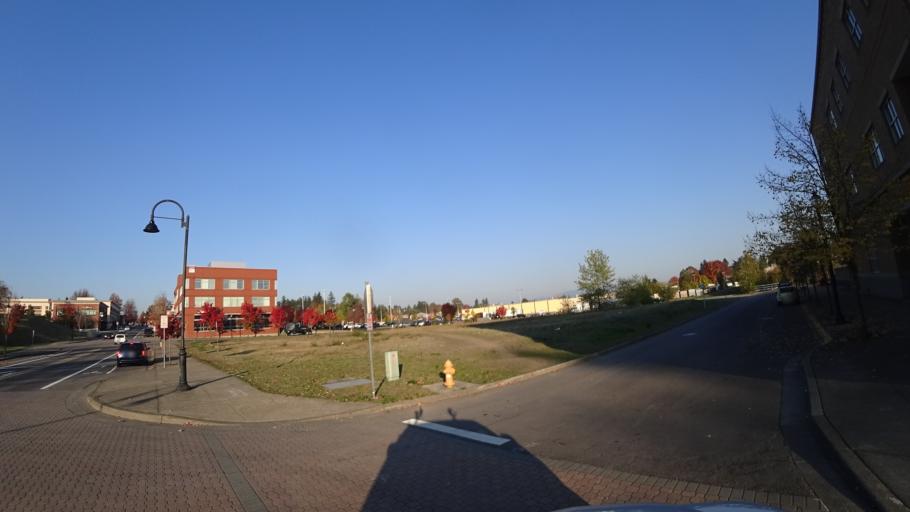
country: US
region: Oregon
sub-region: Multnomah County
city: Gresham
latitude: 45.5084
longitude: -122.4407
